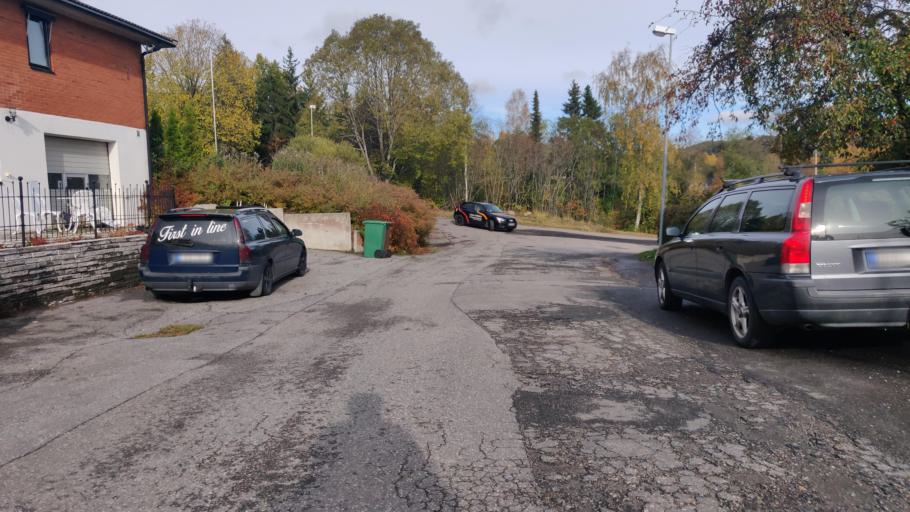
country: SE
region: Vaesternorrland
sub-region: Sundsvalls Kommun
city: Sundsvall
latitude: 62.4163
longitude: 17.3372
